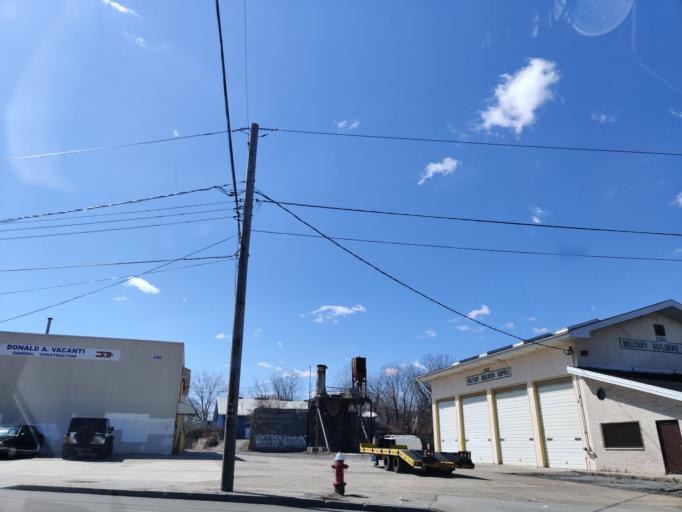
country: US
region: New York
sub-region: Erie County
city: Kenmore
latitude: 42.9434
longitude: -78.8916
